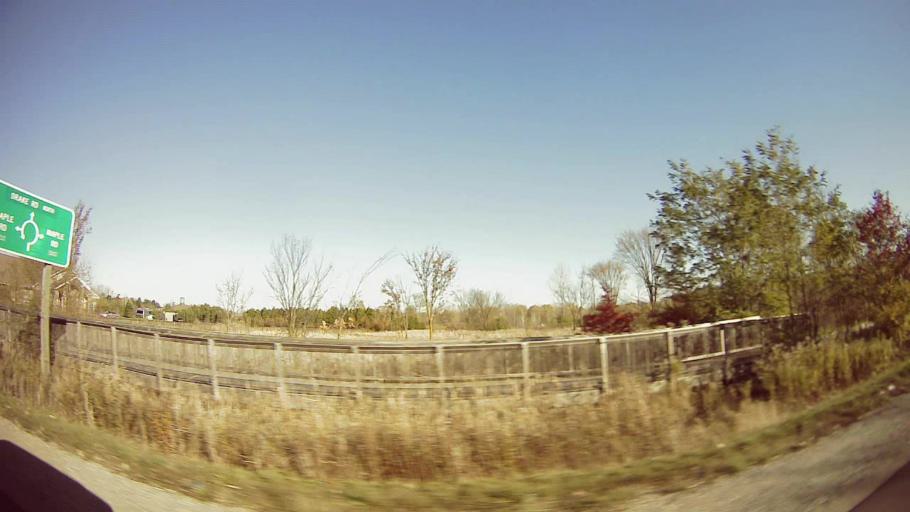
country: US
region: Michigan
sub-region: Oakland County
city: West Bloomfield Township
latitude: 42.5395
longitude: -83.3998
